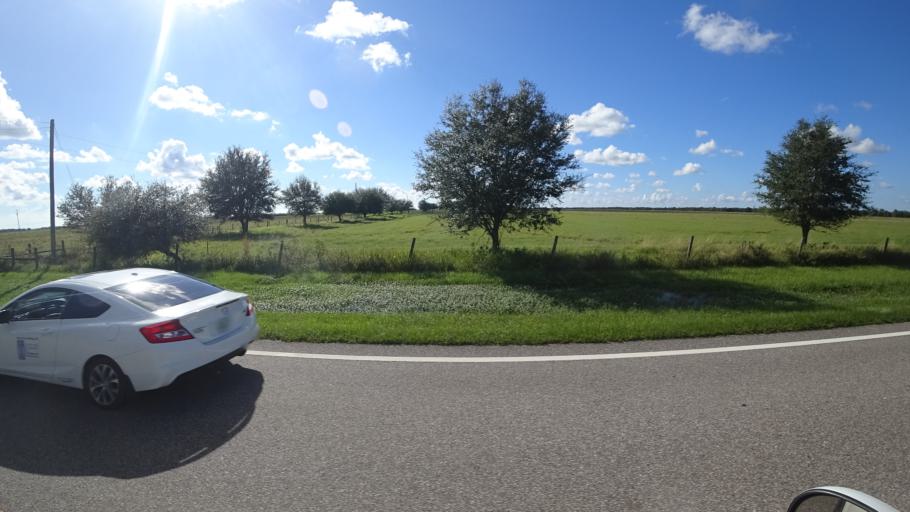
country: US
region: Florida
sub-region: Sarasota County
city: Lake Sarasota
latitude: 27.3718
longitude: -82.2683
